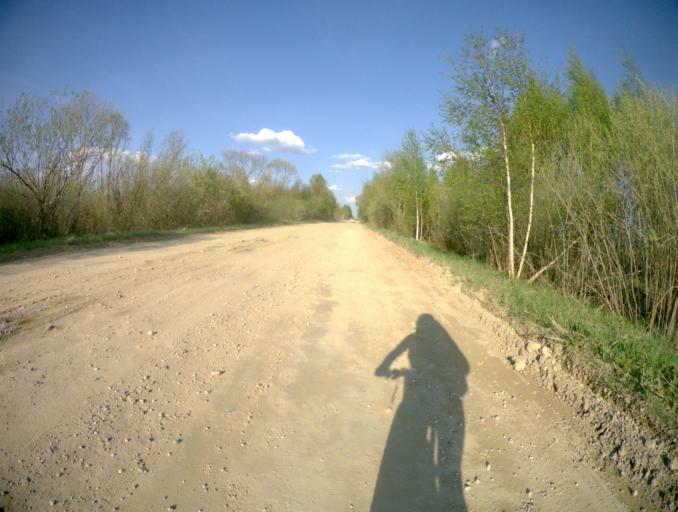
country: RU
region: Vladimir
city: Mstera
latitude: 56.5495
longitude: 41.6808
